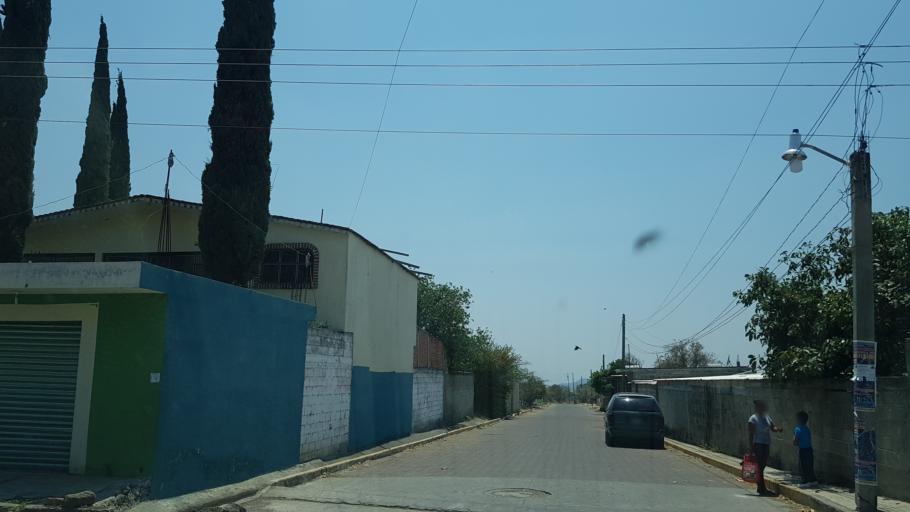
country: MX
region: Puebla
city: Huaquechula
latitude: 18.7696
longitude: -98.5465
